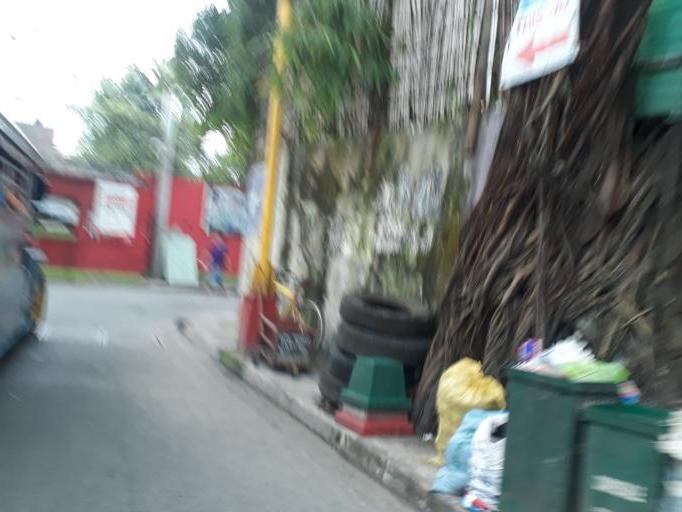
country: PH
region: Calabarzon
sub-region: Province of Rizal
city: Navotas
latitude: 14.6557
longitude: 120.9475
